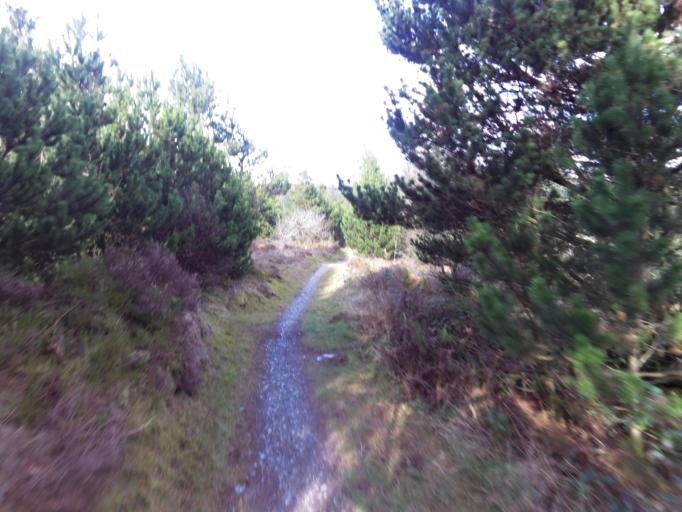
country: GB
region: Wales
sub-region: County of Ceredigion
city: Bow Street
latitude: 52.4229
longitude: -3.8831
